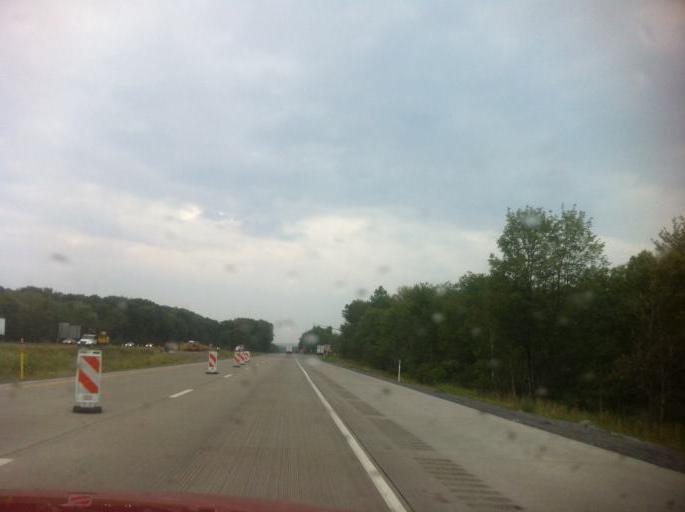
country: US
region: Pennsylvania
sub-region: Jefferson County
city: Reynoldsville
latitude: 41.1508
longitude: -78.9344
